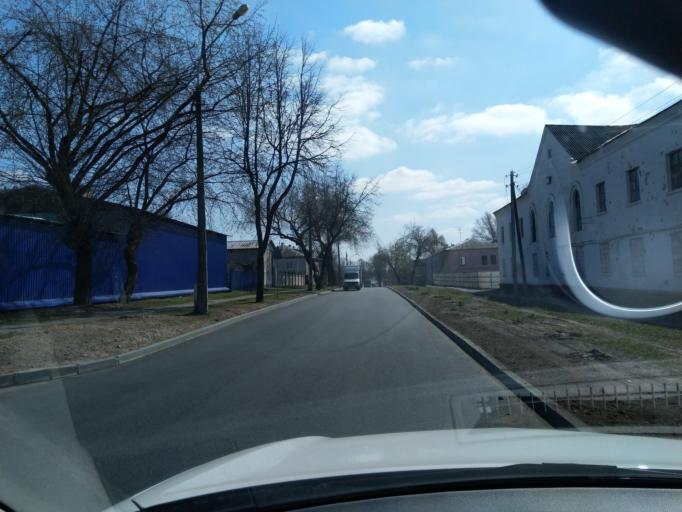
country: BY
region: Minsk
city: Syenitsa
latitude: 53.8715
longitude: 27.5115
